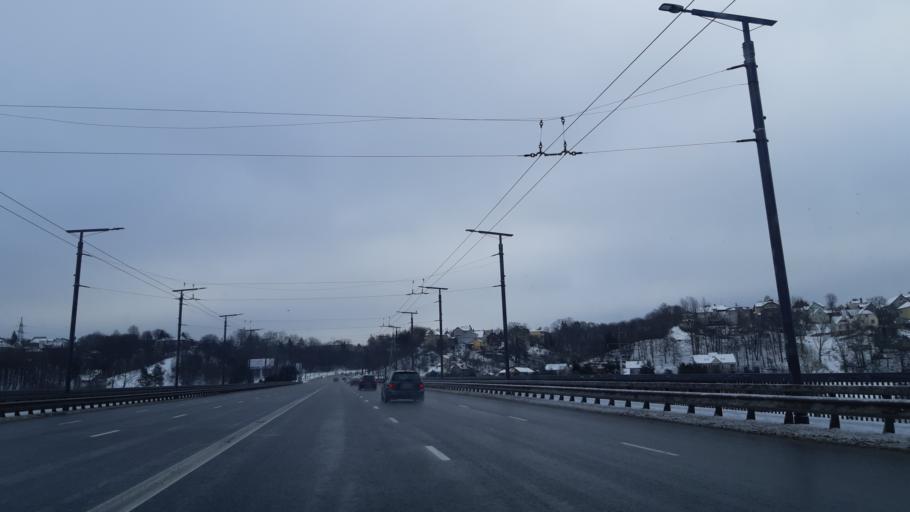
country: LT
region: Kauno apskritis
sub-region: Kaunas
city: Kaunas
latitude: 54.9144
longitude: 23.9077
